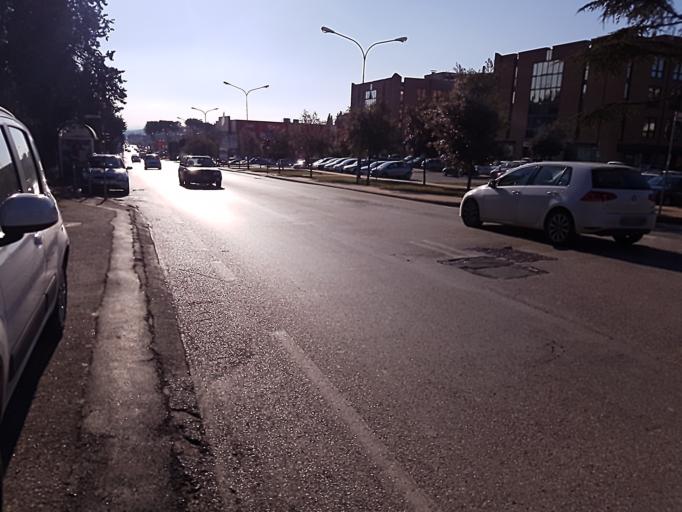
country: IT
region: Umbria
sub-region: Provincia di Perugia
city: Perugia
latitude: 43.0960
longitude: 12.3706
